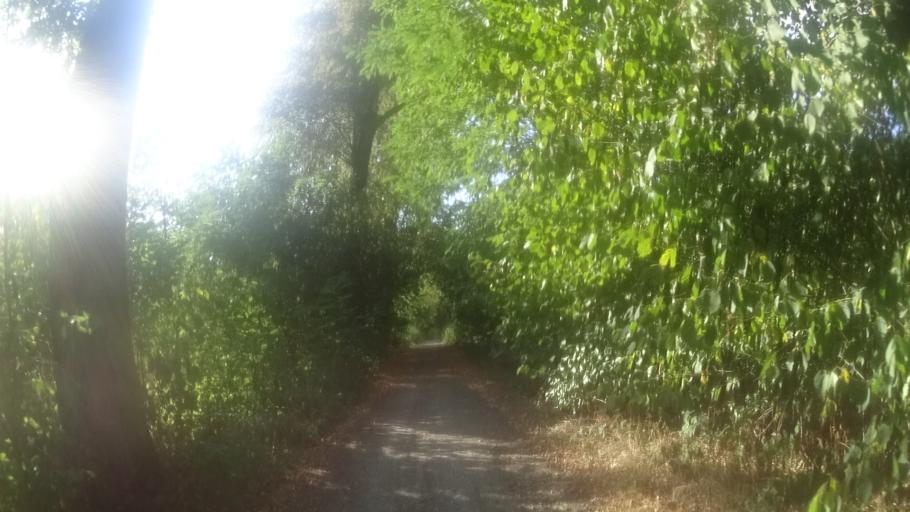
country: CZ
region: Kralovehradecky
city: Trebechovice pod Orebem
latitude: 50.1868
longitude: 16.0110
